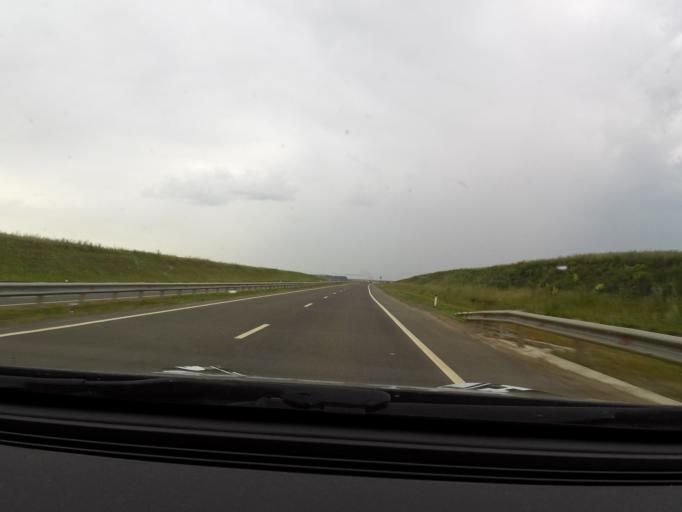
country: RU
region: Bashkortostan
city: Kushnarenkovo
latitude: 55.0673
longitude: 55.3012
